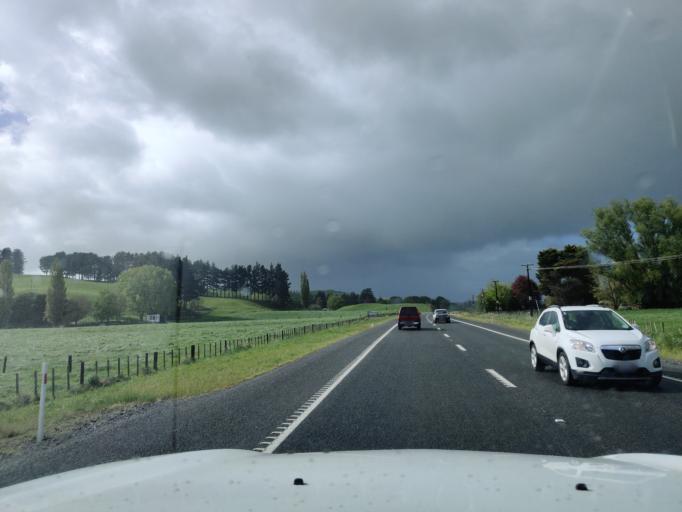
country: NZ
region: Waikato
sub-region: Matamata-Piako District
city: Matamata
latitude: -37.9581
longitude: 175.6855
